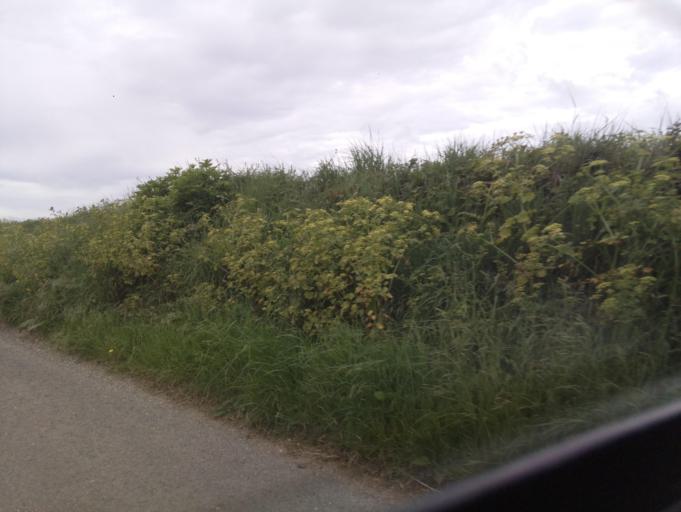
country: GB
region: England
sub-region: Devon
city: Dartmouth
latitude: 50.3404
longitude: -3.6541
